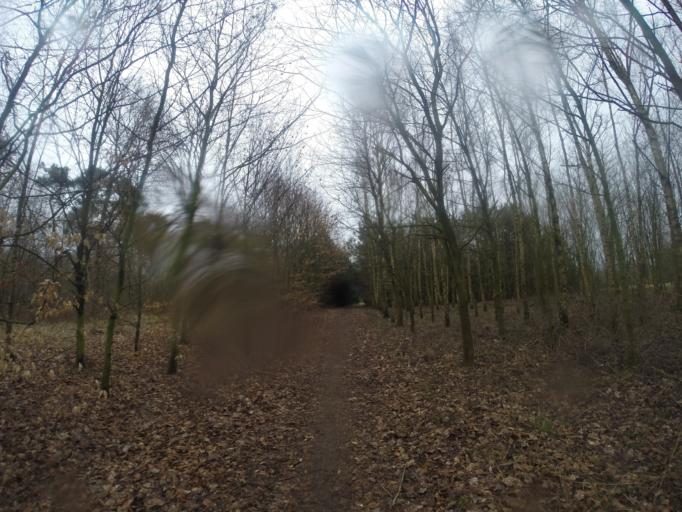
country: NL
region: Gelderland
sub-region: Gemeente Bronckhorst
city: Zelhem
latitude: 52.0192
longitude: 6.3293
